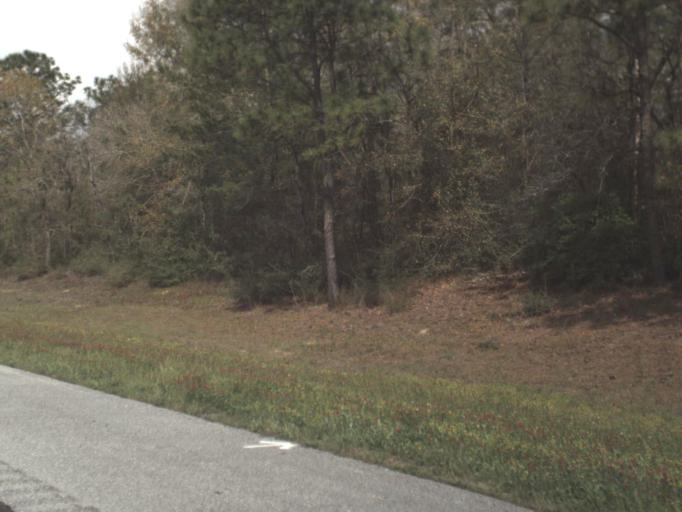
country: US
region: Florida
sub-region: Okaloosa County
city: Crestview
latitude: 30.7165
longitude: -86.6636
